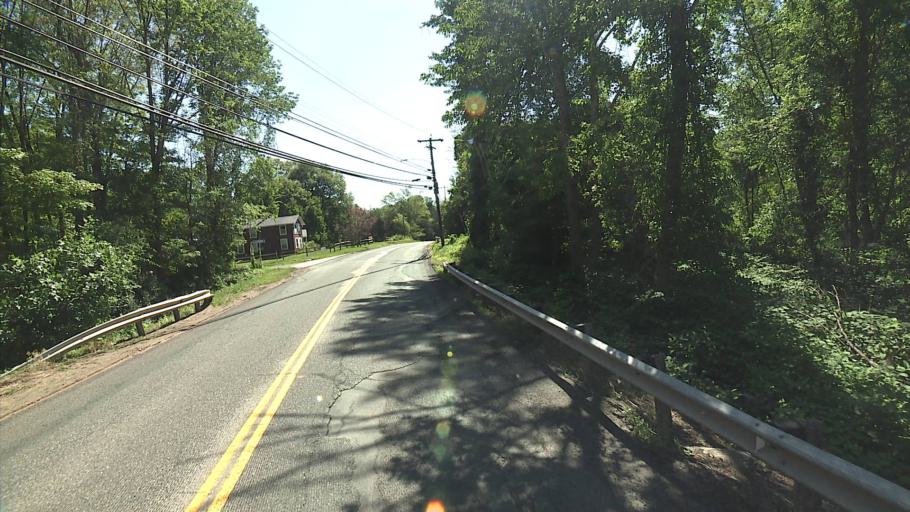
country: US
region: Connecticut
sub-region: Middlesex County
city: East Hampton
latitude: 41.5655
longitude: -72.4734
